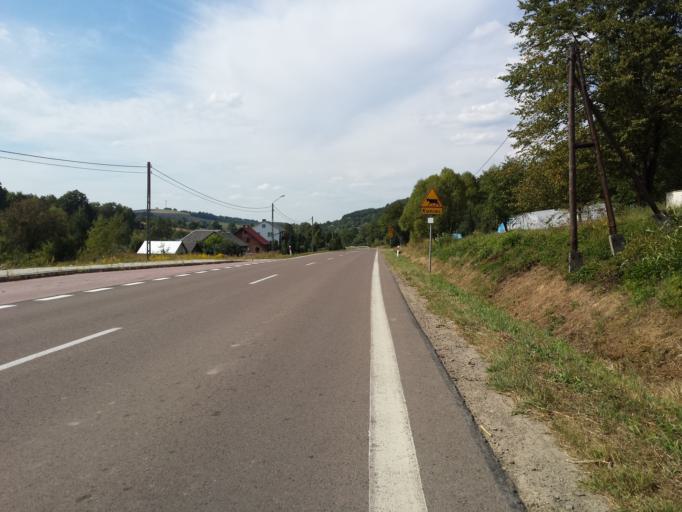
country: PL
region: Subcarpathian Voivodeship
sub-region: Powiat bieszczadzki
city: Ustrzyki Dolne
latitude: 49.5488
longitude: 22.5793
